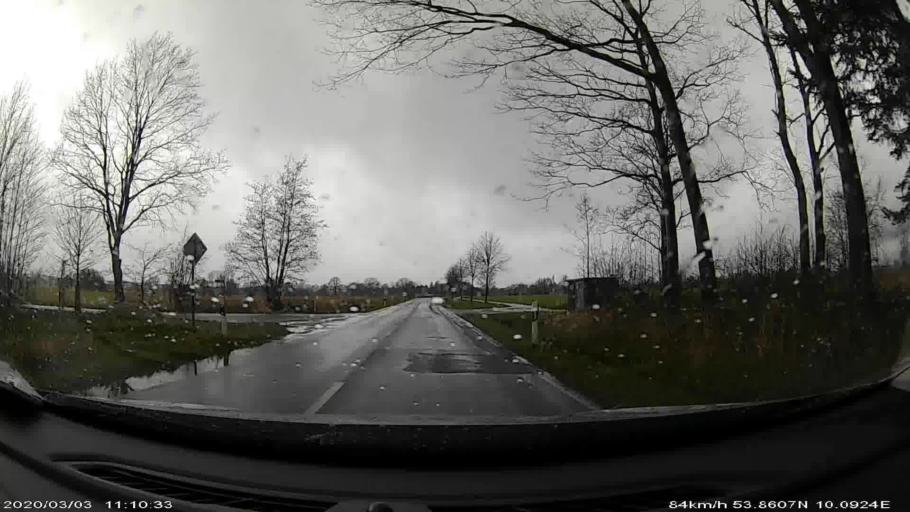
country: DE
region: Schleswig-Holstein
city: Sievershutten
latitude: 53.8624
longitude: 10.0872
